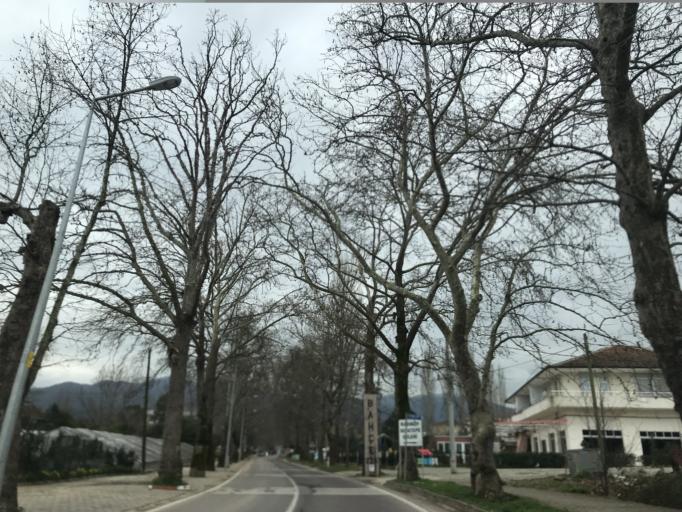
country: TR
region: Yalova
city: Kadikoy
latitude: 40.6126
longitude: 29.2118
